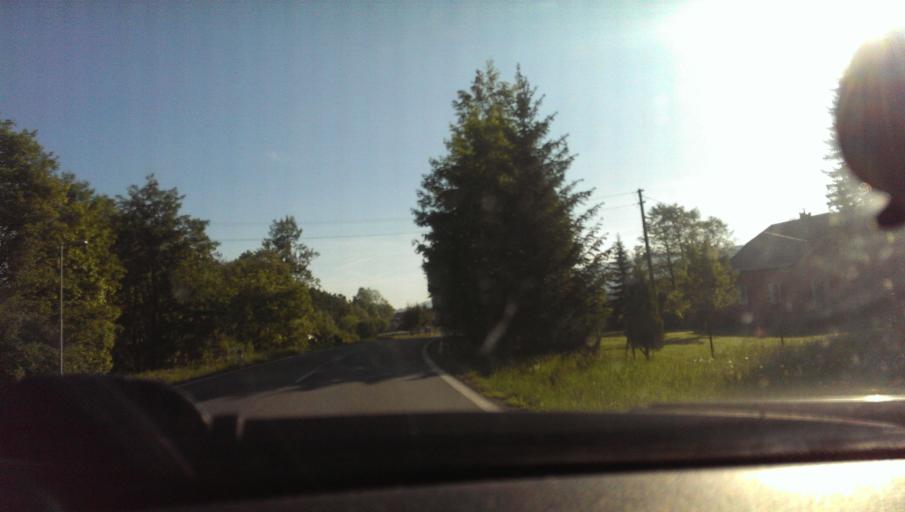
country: CZ
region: Moravskoslezsky
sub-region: Okres Frydek-Mistek
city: Celadna
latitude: 49.5432
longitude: 18.3245
